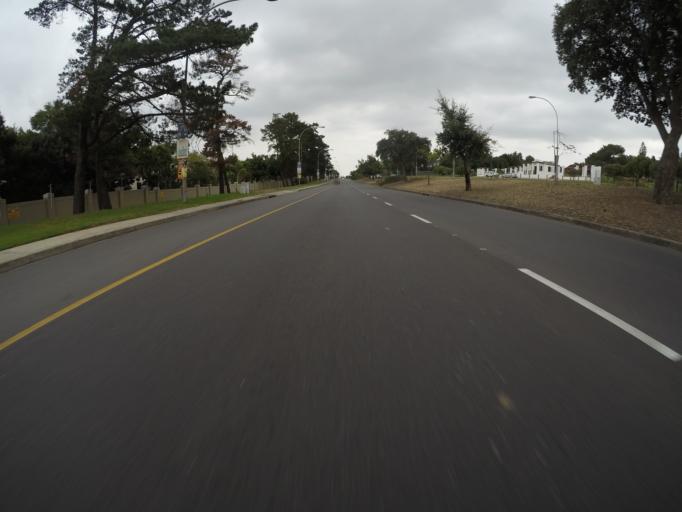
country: ZA
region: Western Cape
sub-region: City of Cape Town
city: Kraaifontein
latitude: -33.8499
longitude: 18.6442
